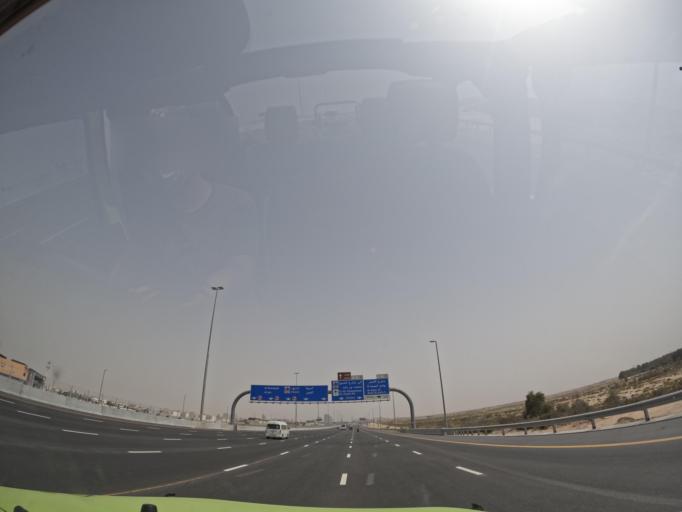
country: AE
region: Dubai
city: Dubai
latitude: 25.1442
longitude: 55.3443
